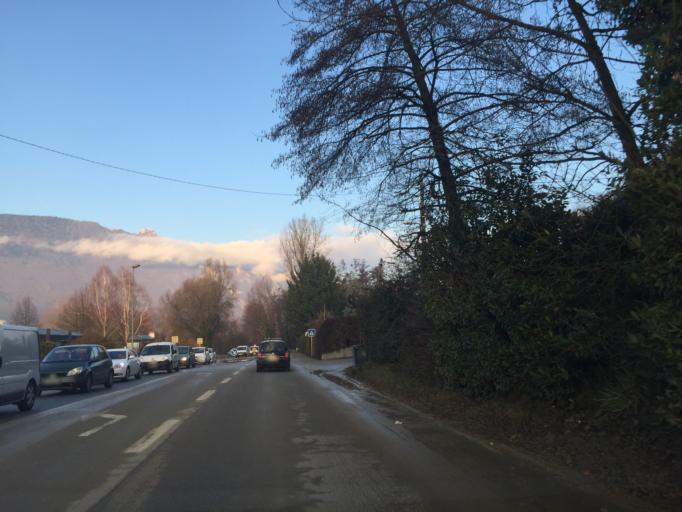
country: FR
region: Rhone-Alpes
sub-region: Departement de la Savoie
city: Viviers-du-Lac
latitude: 45.6472
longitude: 5.8962
